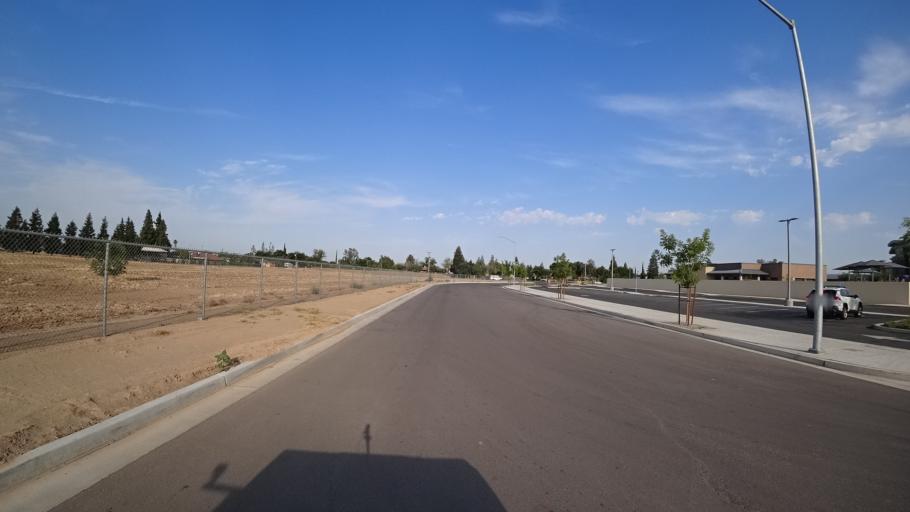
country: US
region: California
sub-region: Fresno County
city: West Park
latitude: 36.7683
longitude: -119.8512
